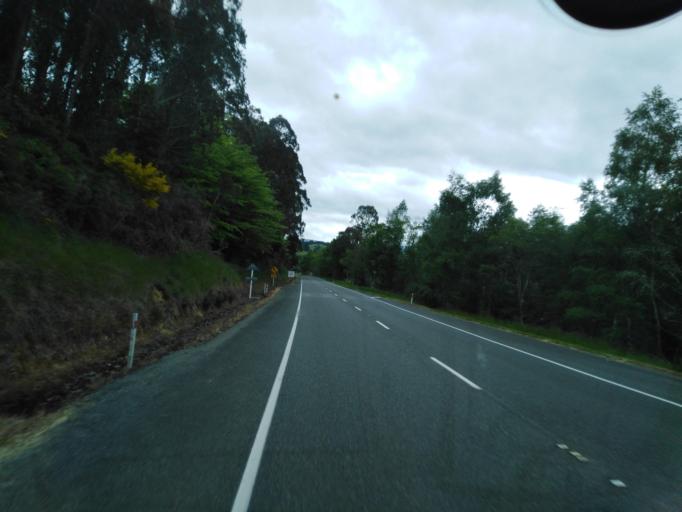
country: NZ
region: Tasman
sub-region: Tasman District
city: Wakefield
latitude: -41.6321
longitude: 172.6940
